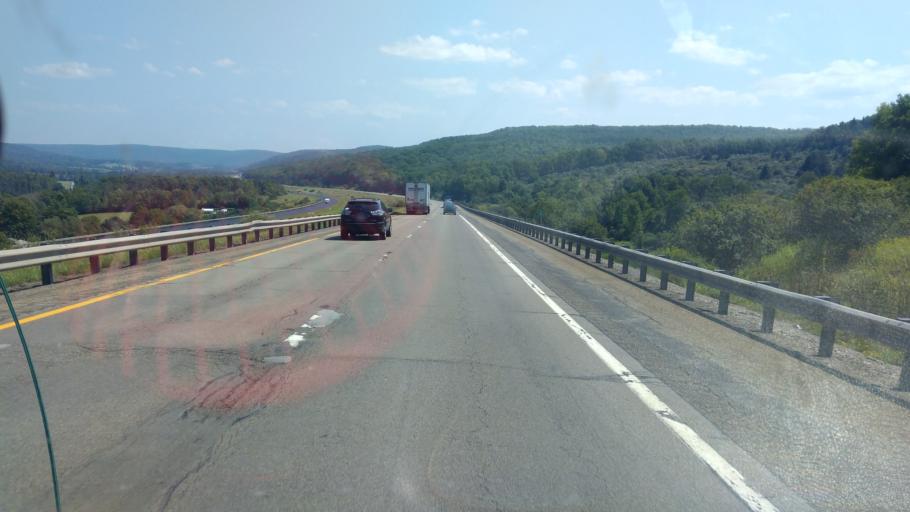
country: US
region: New York
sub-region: Allegany County
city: Alfred
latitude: 42.3190
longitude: -77.8266
